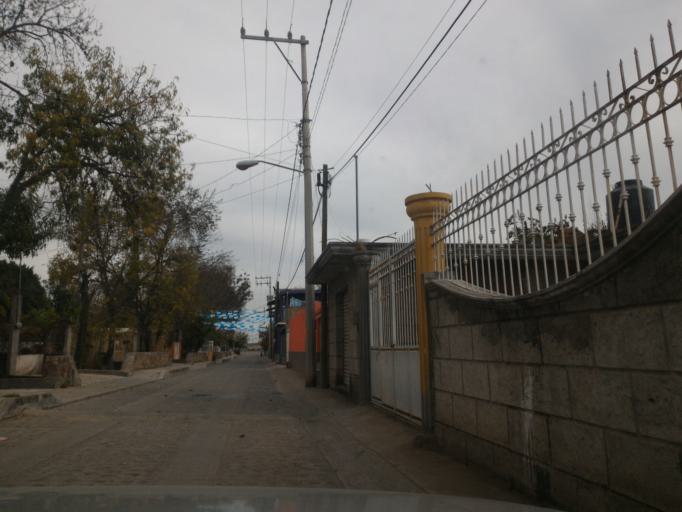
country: MX
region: Jalisco
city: San Diego de Alejandria
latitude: 20.8848
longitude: -101.9791
